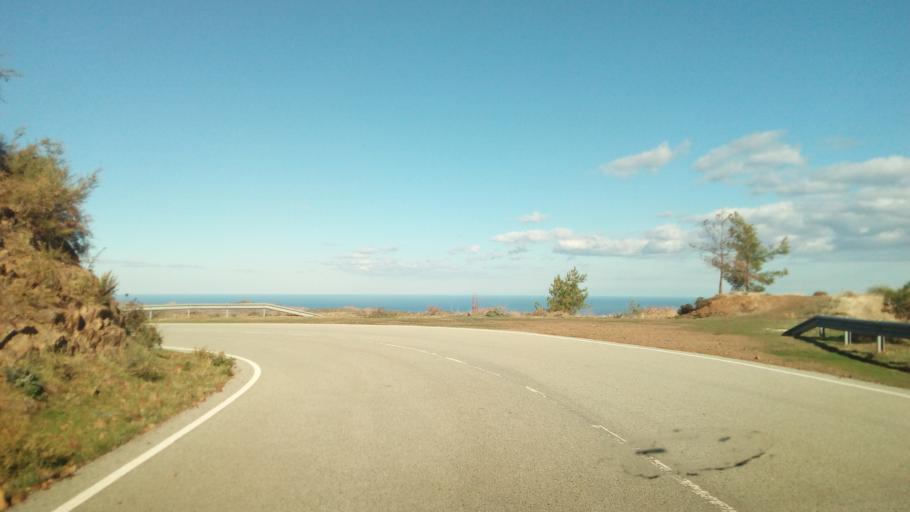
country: CY
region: Lefkosia
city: Lefka
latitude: 35.1073
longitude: 32.7749
